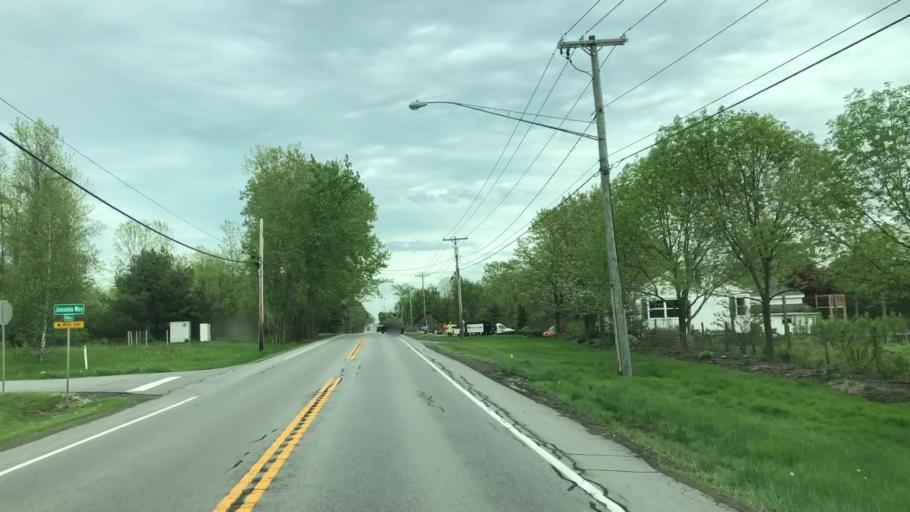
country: US
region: New York
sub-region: Monroe County
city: Fairport
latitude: 43.1307
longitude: -77.3876
